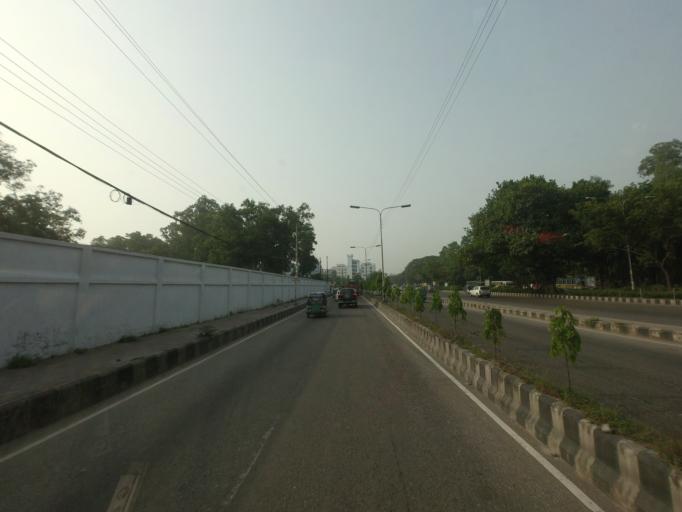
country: BD
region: Dhaka
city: Azimpur
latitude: 23.7668
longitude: 90.3833
